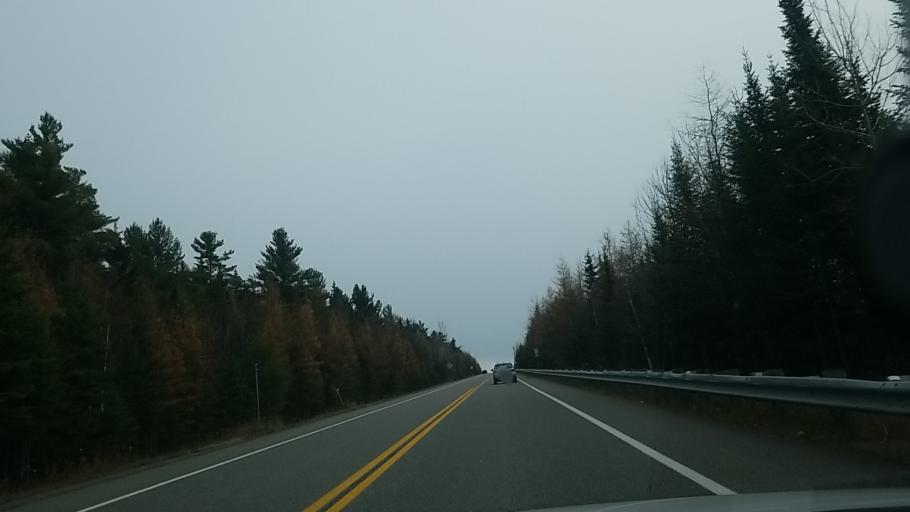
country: CA
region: Quebec
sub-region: Laurentides
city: Saint-Sauveur
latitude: 45.8157
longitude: -74.2485
